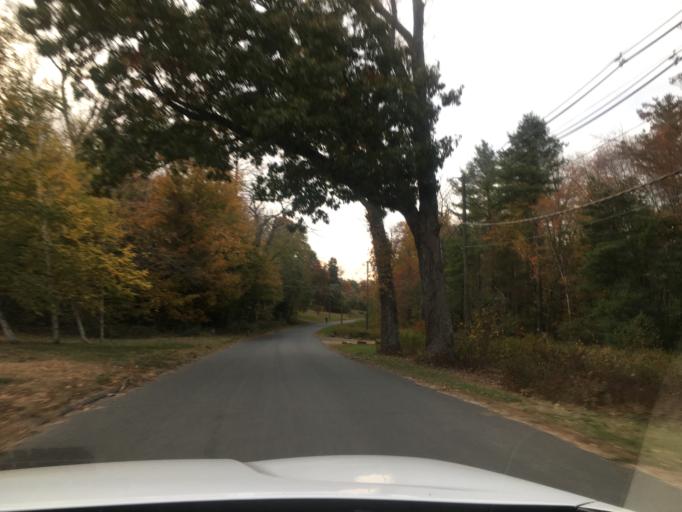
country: US
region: Connecticut
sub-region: Hartford County
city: Hazardville
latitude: 41.9779
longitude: -72.5052
